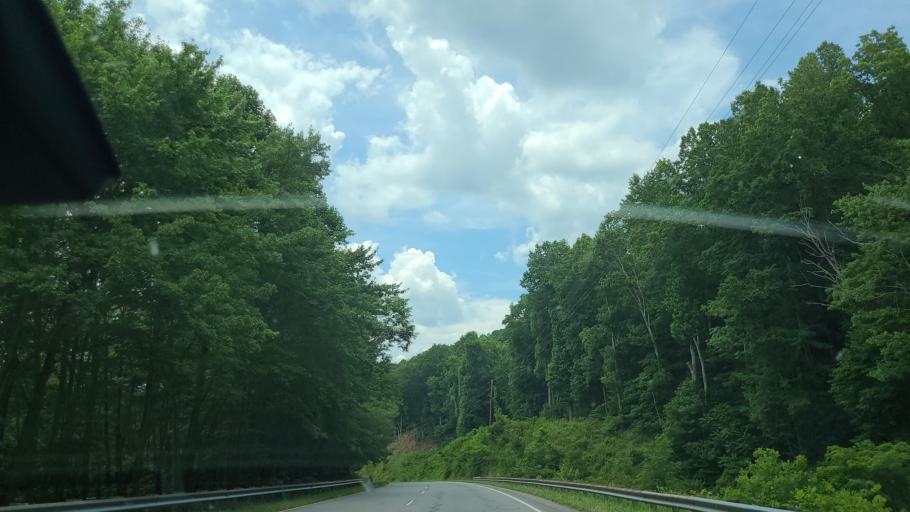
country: US
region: Georgia
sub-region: Fannin County
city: McCaysville
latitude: 35.0167
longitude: -84.2868
